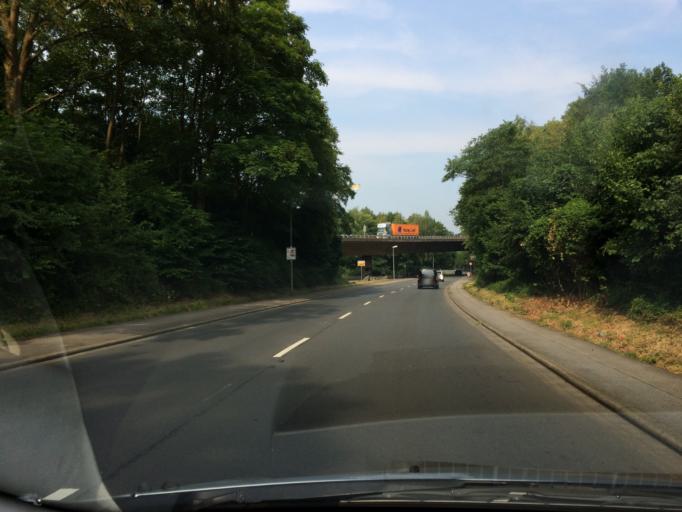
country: DE
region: North Rhine-Westphalia
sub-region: Regierungsbezirk Arnsberg
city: Nachrodt-Wiblingwerde
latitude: 51.3641
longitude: 7.6325
